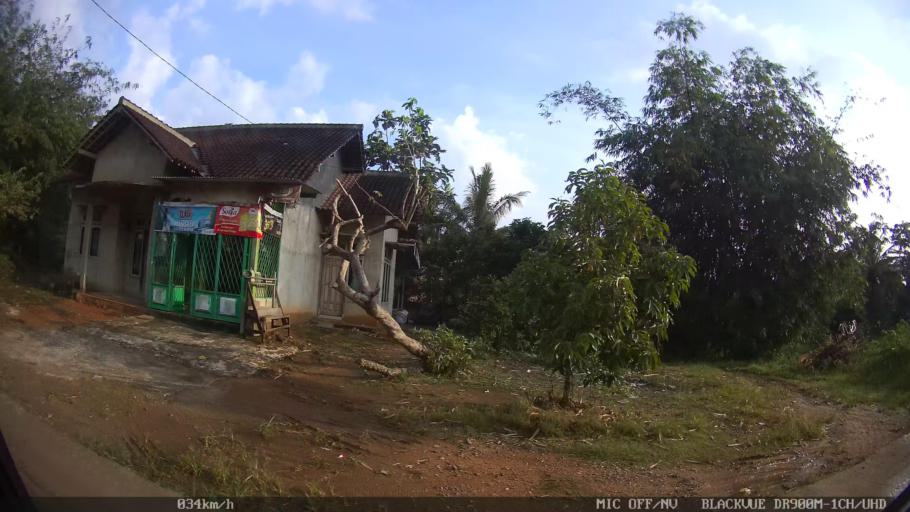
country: ID
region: Lampung
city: Kedaton
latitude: -5.3921
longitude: 105.3297
